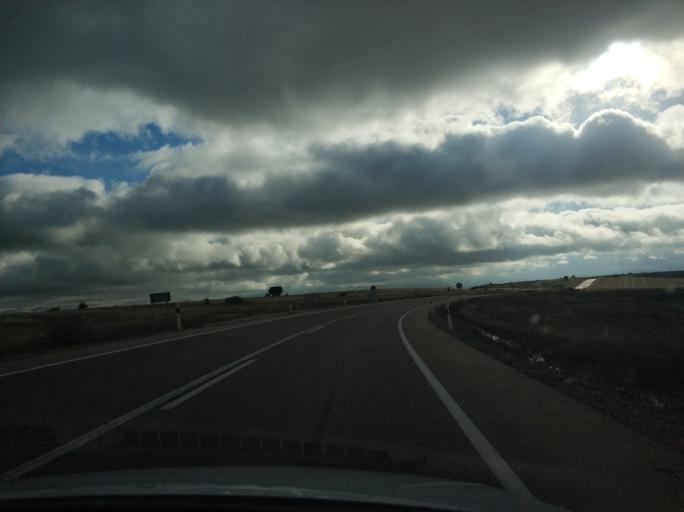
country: ES
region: Castille and Leon
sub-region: Provincia de Soria
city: Fuentecambron
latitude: 41.4724
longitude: -3.3241
